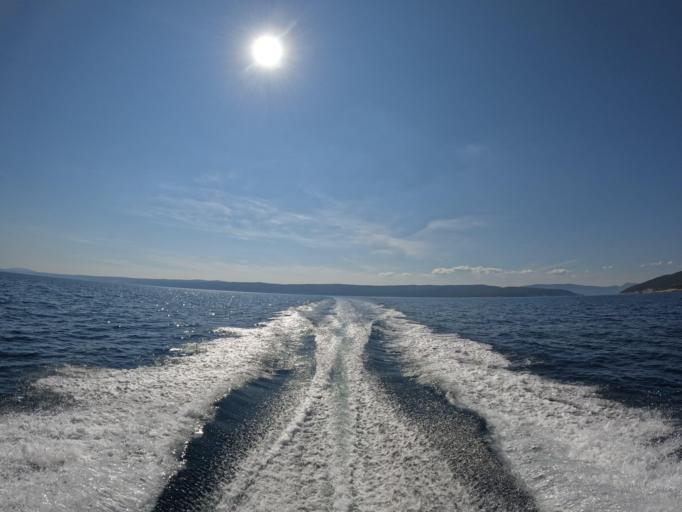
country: HR
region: Primorsko-Goranska
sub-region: Grad Krk
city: Krk
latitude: 44.9488
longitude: 14.5362
